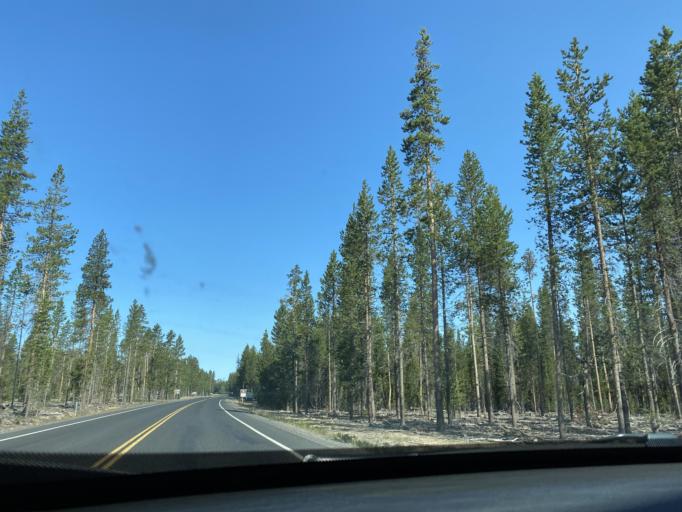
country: US
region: Oregon
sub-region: Deschutes County
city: Three Rivers
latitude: 43.7087
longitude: -121.2716
